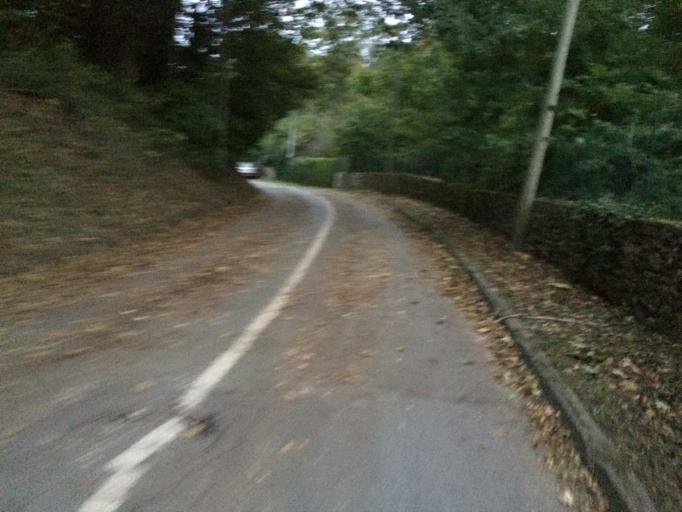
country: FR
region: Ile-de-France
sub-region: Departement de l'Essonne
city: Bievres
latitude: 48.7590
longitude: 2.1988
